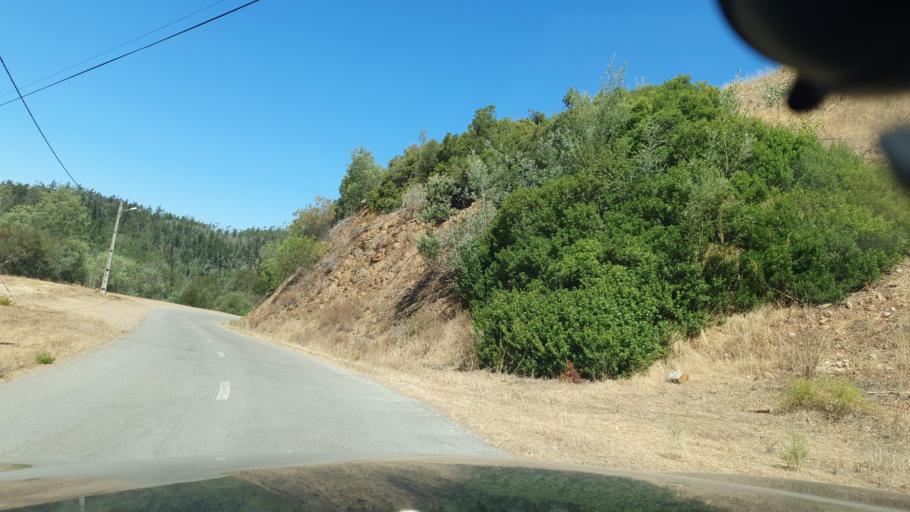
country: PT
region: Beja
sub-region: Odemira
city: Odemira
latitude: 37.5109
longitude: -8.4389
